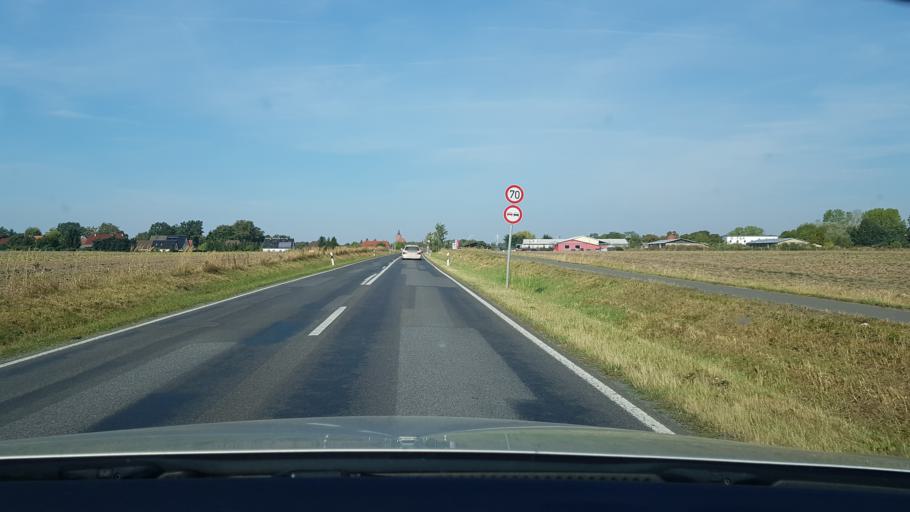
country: DE
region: Brandenburg
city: Beeskow
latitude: 52.1646
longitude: 14.2679
